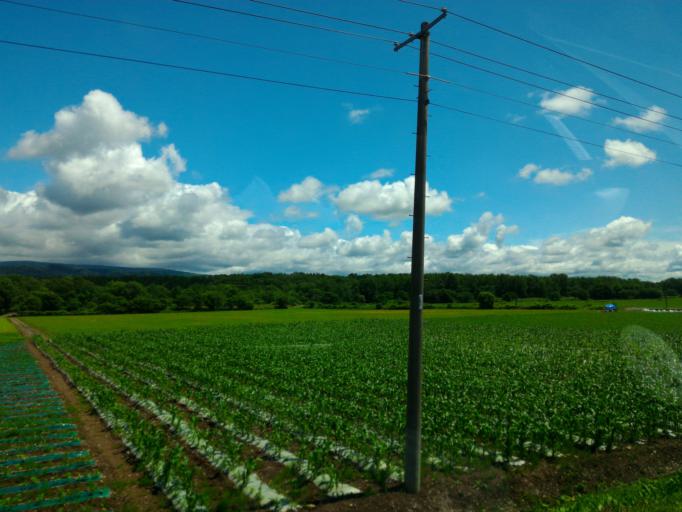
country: JP
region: Hokkaido
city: Nayoro
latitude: 44.5231
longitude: 142.3265
